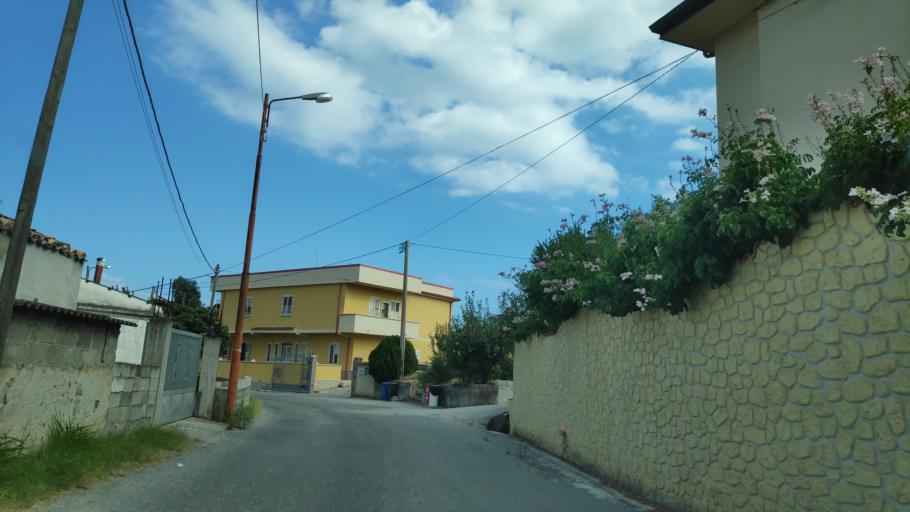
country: IT
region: Calabria
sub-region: Provincia di Catanzaro
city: Guardavalle Marina
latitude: 38.4627
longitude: 16.5765
